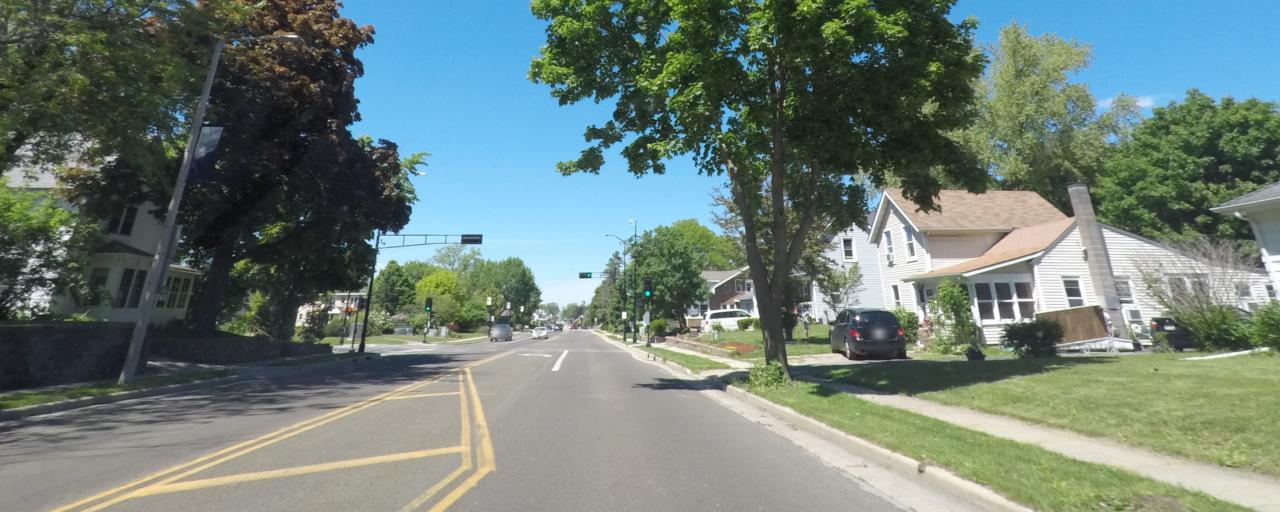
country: US
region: Wisconsin
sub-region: Dane County
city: Verona
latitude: 42.9850
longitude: -89.5334
